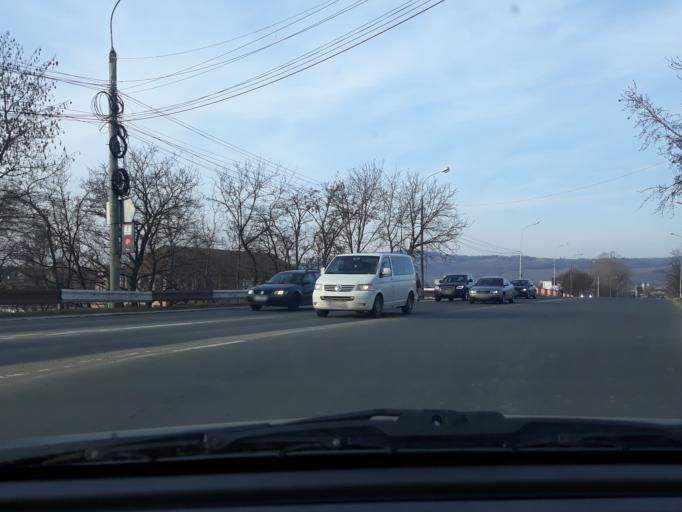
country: RO
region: Salaj
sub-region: Comuna Criseni
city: Criseni
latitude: 47.2169
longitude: 23.0418
